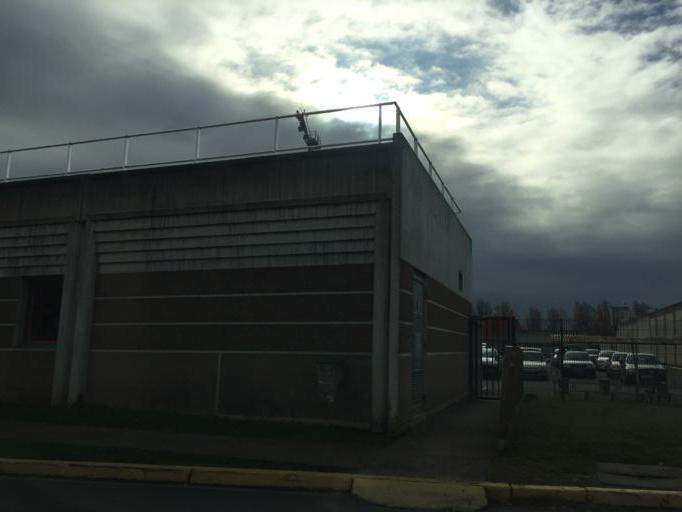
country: FR
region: Rhone-Alpes
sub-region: Departement du Rhone
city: Villefranche-sur-Saone
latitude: 45.9977
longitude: 4.7266
